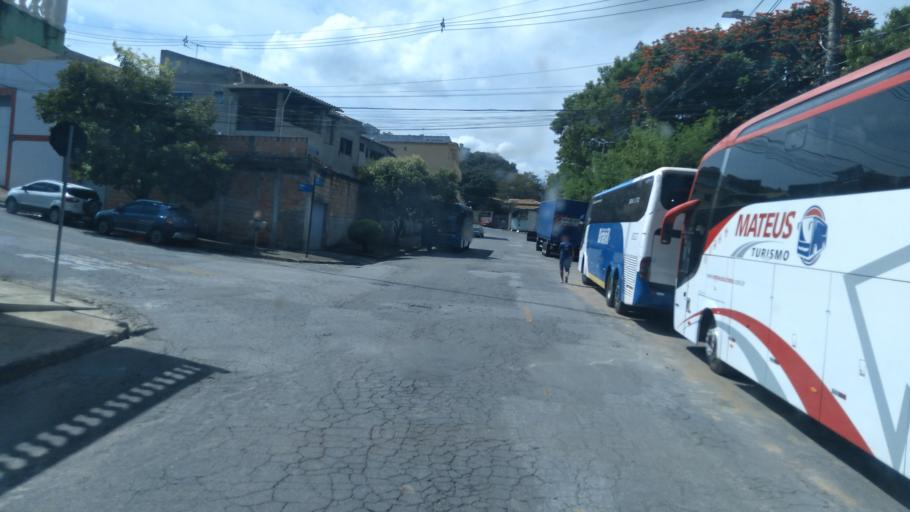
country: BR
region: Minas Gerais
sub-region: Belo Horizonte
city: Belo Horizonte
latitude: -19.8589
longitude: -43.8958
